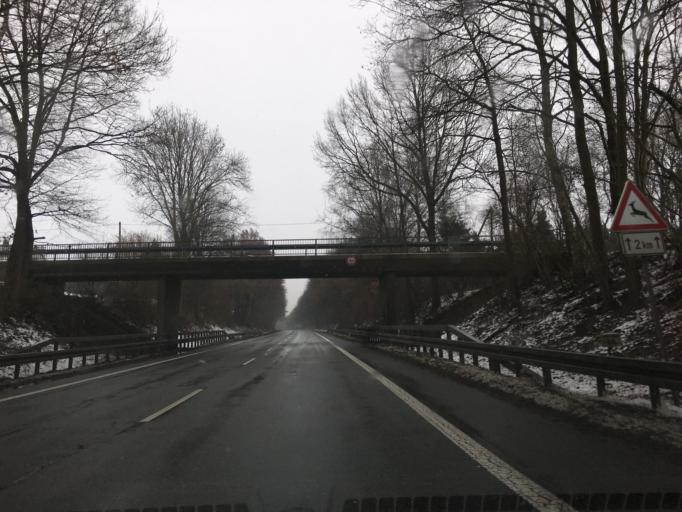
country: DE
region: North Rhine-Westphalia
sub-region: Regierungsbezirk Munster
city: Klein Reken
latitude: 51.7891
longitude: 7.0278
